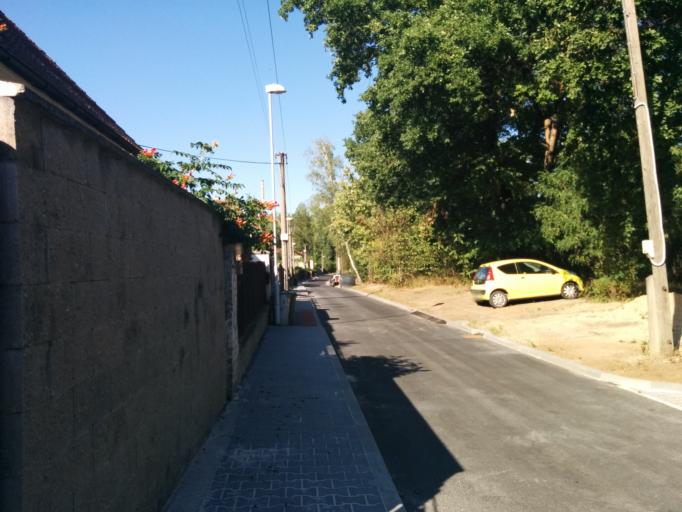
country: CZ
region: Central Bohemia
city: Neratovice
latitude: 50.2647
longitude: 14.5124
